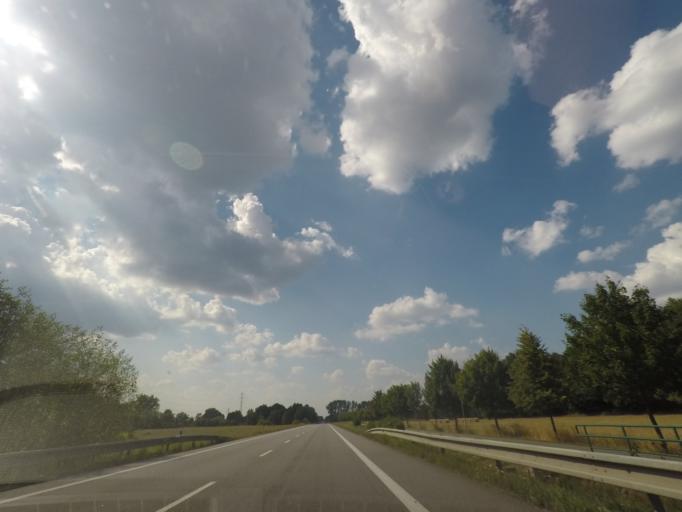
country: CZ
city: Albrechtice nad Orlici
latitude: 50.1622
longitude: 16.0553
